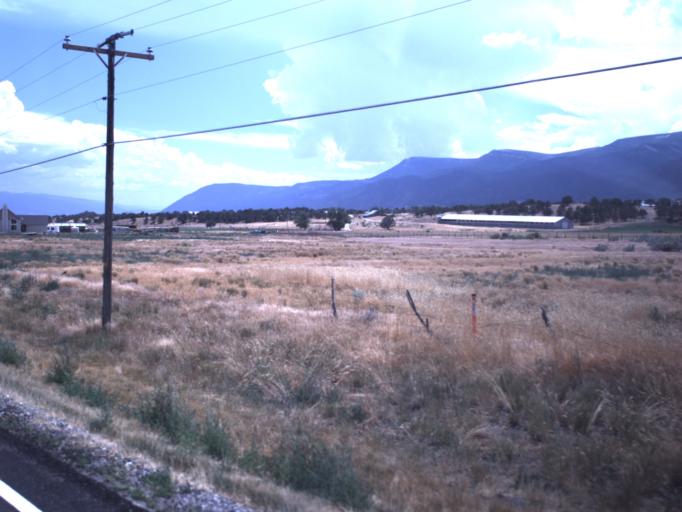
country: US
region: Utah
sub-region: Sanpete County
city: Fountain Green
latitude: 39.6080
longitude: -111.6255
